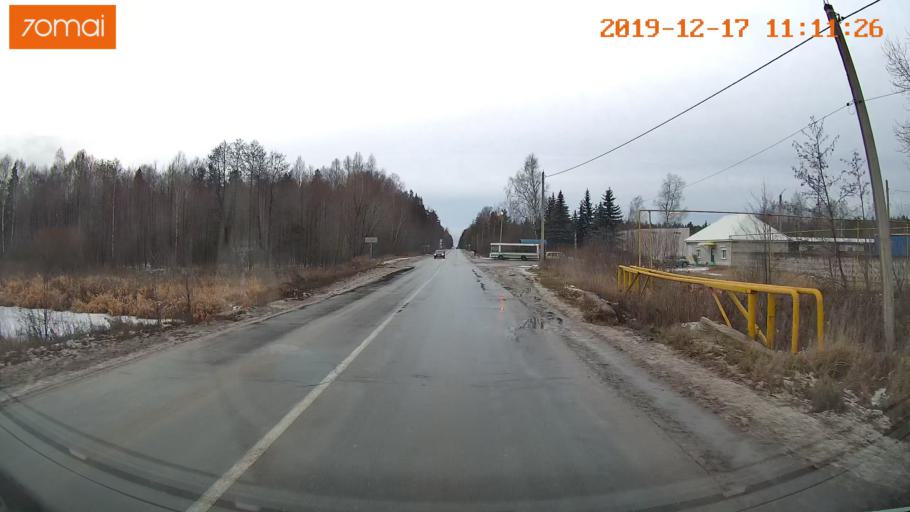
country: RU
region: Vladimir
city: Gus'-Khrustal'nyy
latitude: 55.5866
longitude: 40.6367
